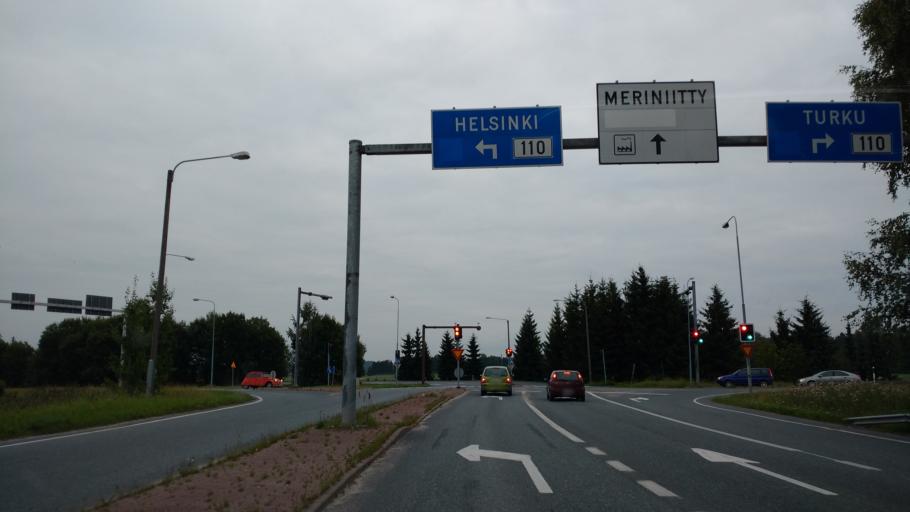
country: FI
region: Varsinais-Suomi
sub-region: Salo
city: Halikko
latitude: 60.3925
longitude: 23.0827
